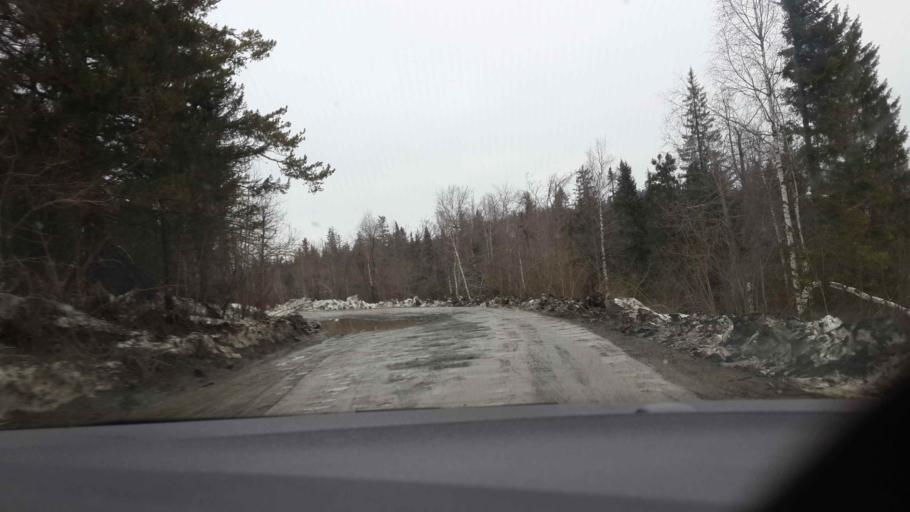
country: RU
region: Chelyabinsk
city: Magnitka
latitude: 55.2710
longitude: 59.6989
